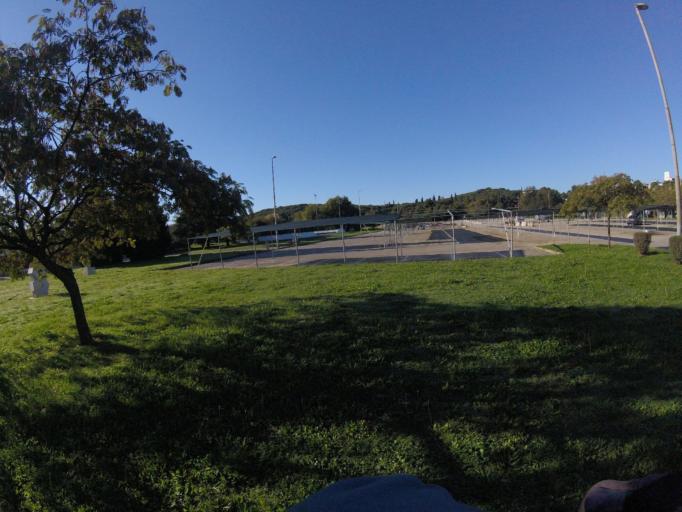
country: HR
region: Istarska
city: Vrsar
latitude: 45.1476
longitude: 13.6057
